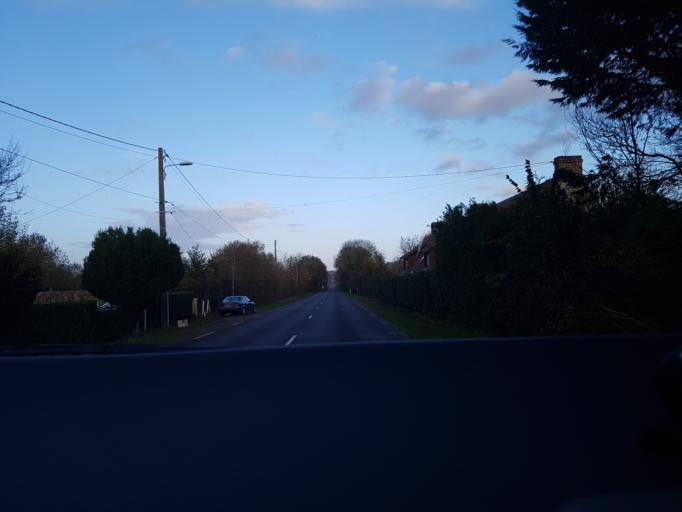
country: FR
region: Lower Normandy
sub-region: Departement du Calvados
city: Dozule
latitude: 49.2195
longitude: -0.0915
